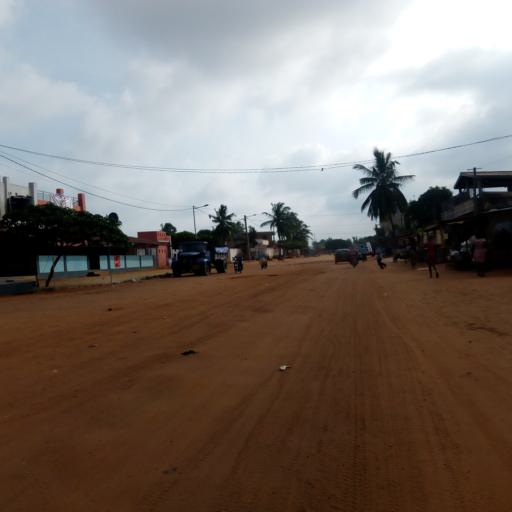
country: TG
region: Maritime
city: Lome
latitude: 6.1838
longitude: 1.1776
